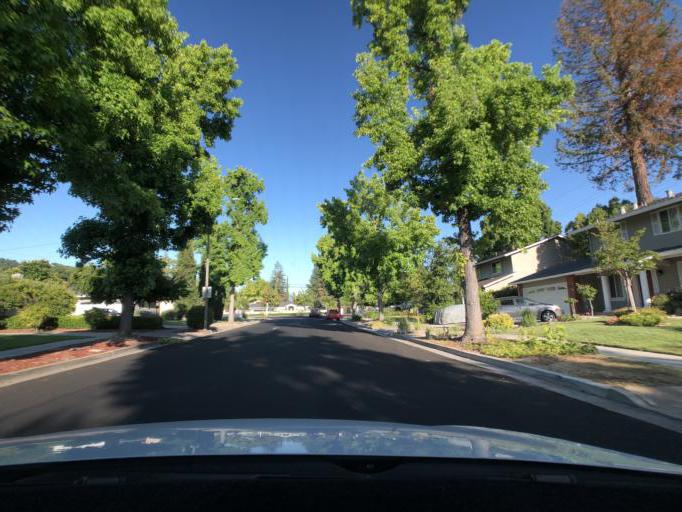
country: US
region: California
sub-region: Santa Clara County
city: Cambrian Park
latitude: 37.2390
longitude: -121.9302
